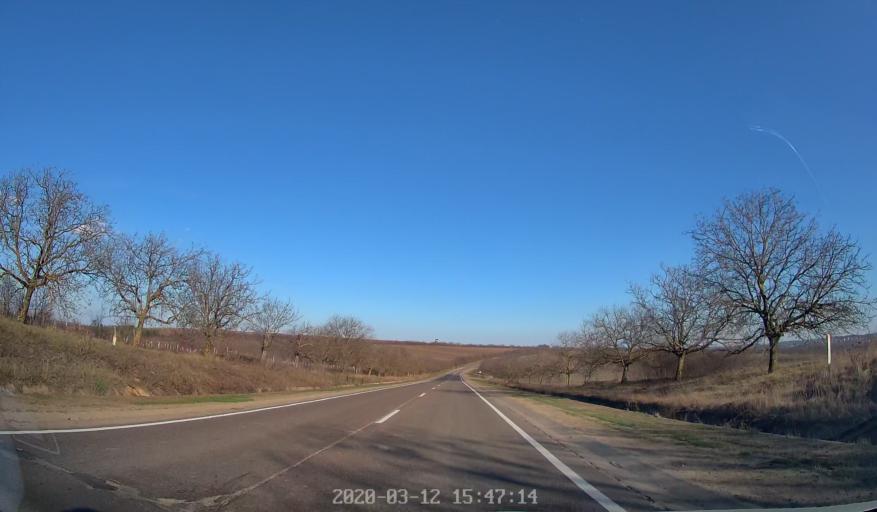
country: MD
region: Chisinau
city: Ciorescu
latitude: 47.0971
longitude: 28.9072
